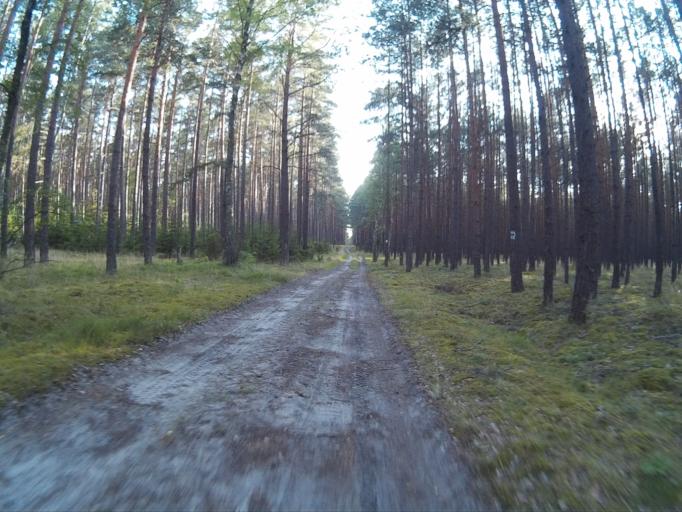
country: PL
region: Kujawsko-Pomorskie
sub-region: Powiat tucholski
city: Cekcyn
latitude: 53.5532
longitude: 18.0963
